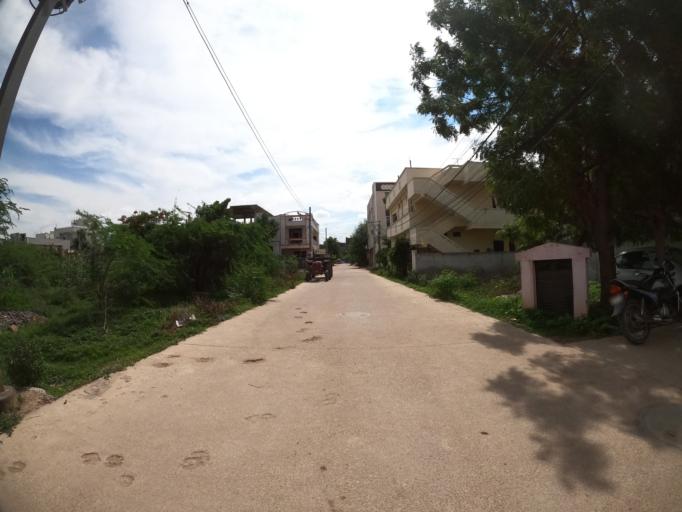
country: IN
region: Telangana
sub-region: Hyderabad
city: Hyderabad
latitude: 17.3649
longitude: 78.3845
